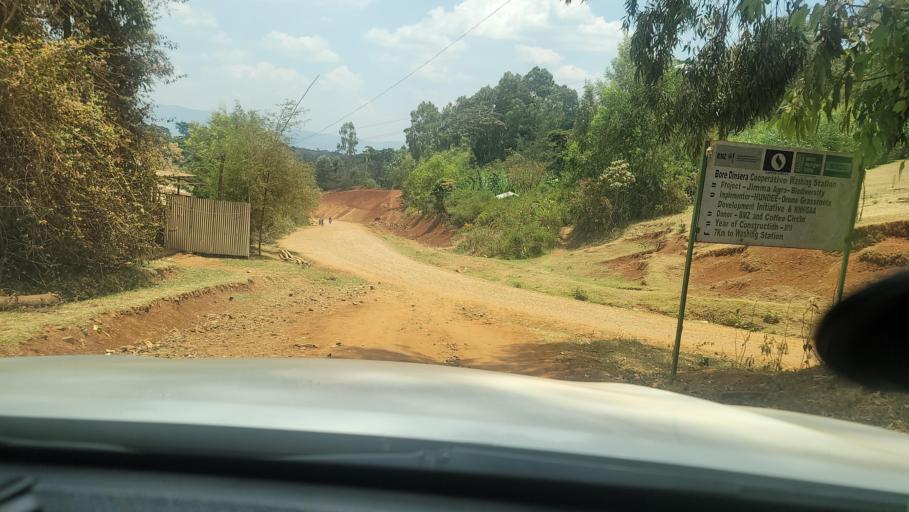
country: ET
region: Oromiya
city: Agaro
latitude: 7.8050
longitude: 36.4653
